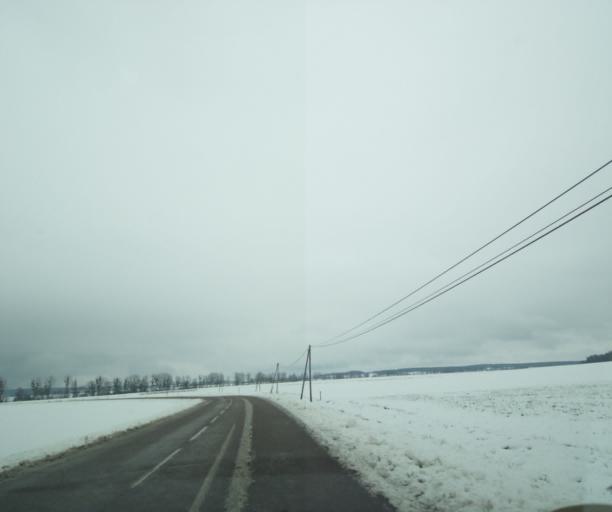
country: FR
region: Champagne-Ardenne
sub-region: Departement de la Haute-Marne
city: Montier-en-Der
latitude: 48.4478
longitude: 4.7848
